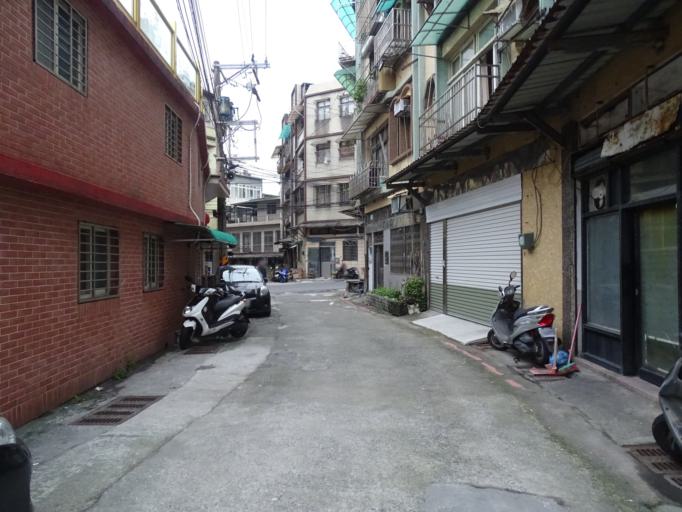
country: TW
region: Taiwan
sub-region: Keelung
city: Keelung
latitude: 25.1553
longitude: 121.7660
